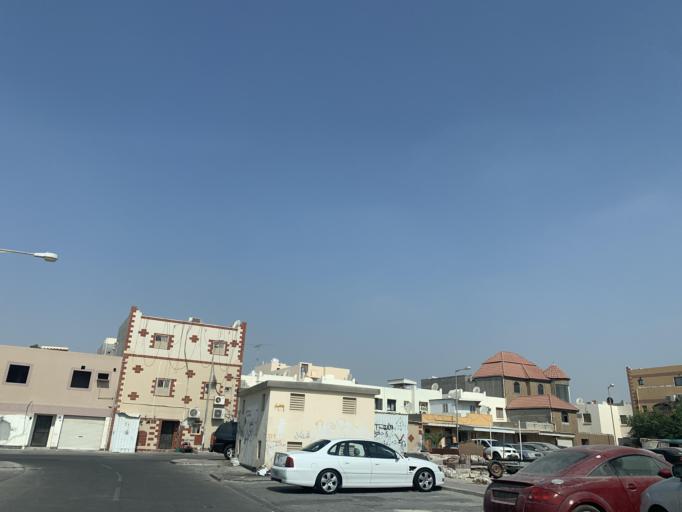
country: BH
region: Central Governorate
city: Madinat Hamad
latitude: 26.1253
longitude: 50.4923
